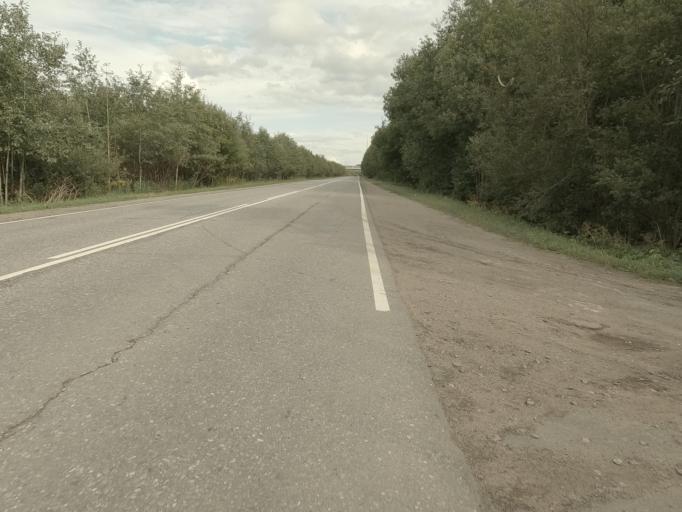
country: RU
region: Leningrad
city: Mga
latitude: 59.7610
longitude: 31.0067
